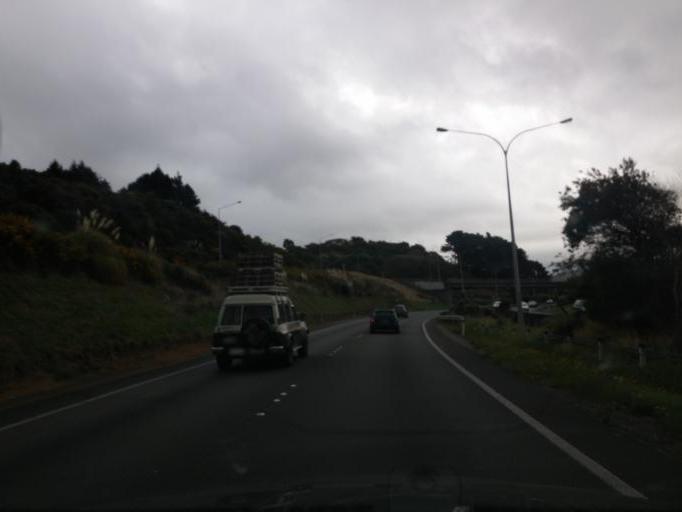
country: NZ
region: Wellington
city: Petone
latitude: -41.2031
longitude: 174.8223
